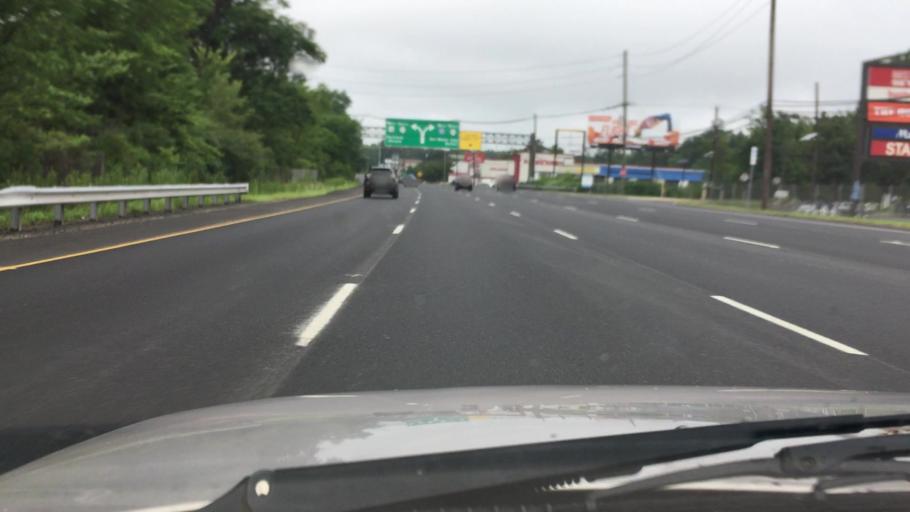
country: US
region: New Jersey
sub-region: Passaic County
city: Singac
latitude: 40.8952
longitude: -74.2384
